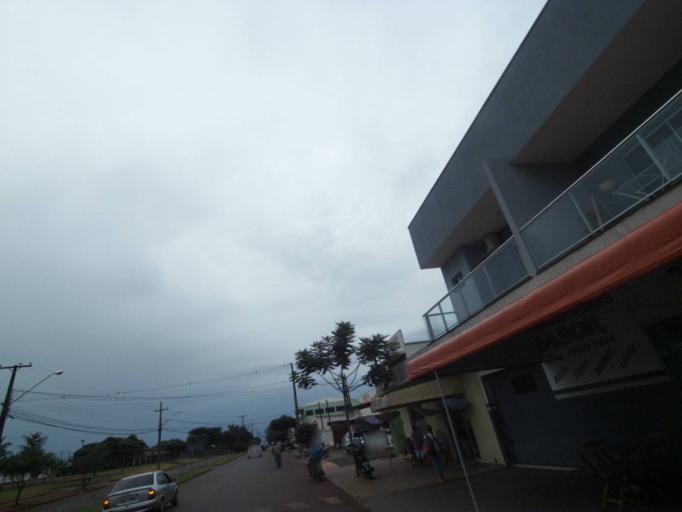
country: BR
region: Parana
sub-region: Campo Mourao
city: Campo Mourao
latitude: -24.0196
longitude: -52.3555
